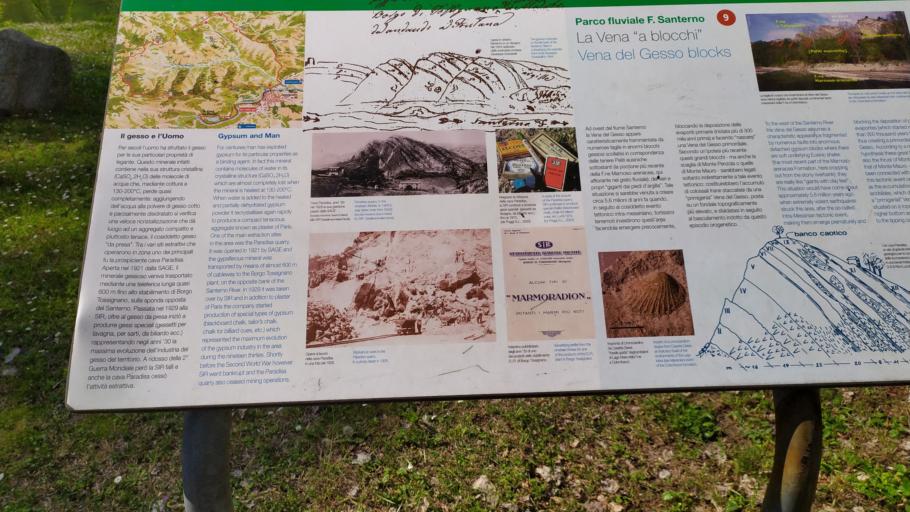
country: IT
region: Emilia-Romagna
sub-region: Provincia di Bologna
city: Borgo Tossignano
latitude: 44.2763
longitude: 11.5853
